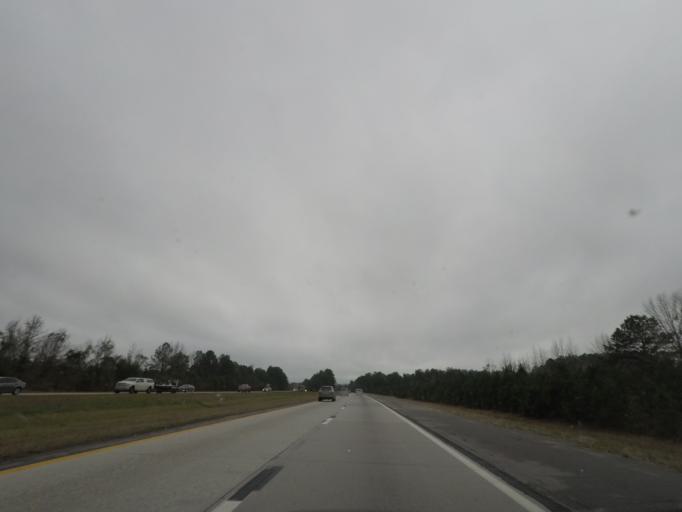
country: US
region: South Carolina
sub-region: Dorchester County
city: Saint George
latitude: 33.1289
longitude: -80.6387
